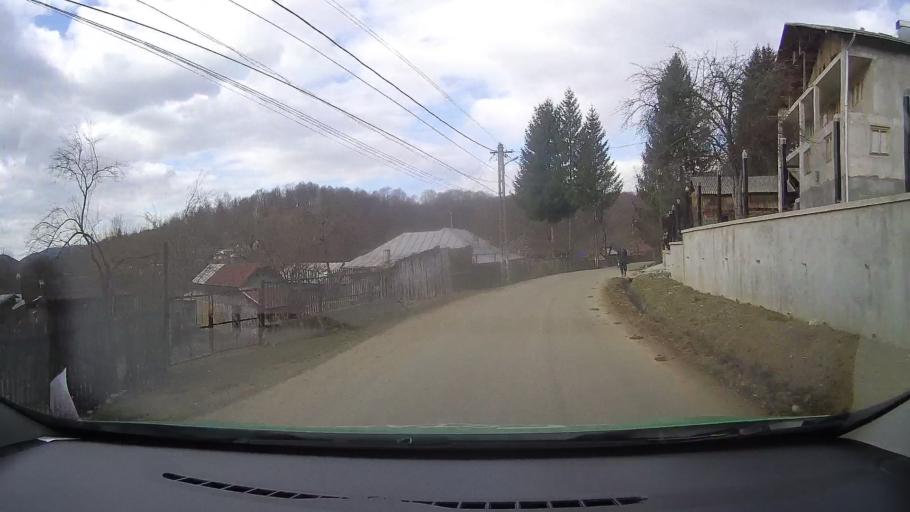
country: RO
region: Prahova
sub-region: Comuna Adunati
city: Adunati
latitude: 45.1176
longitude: 25.5898
